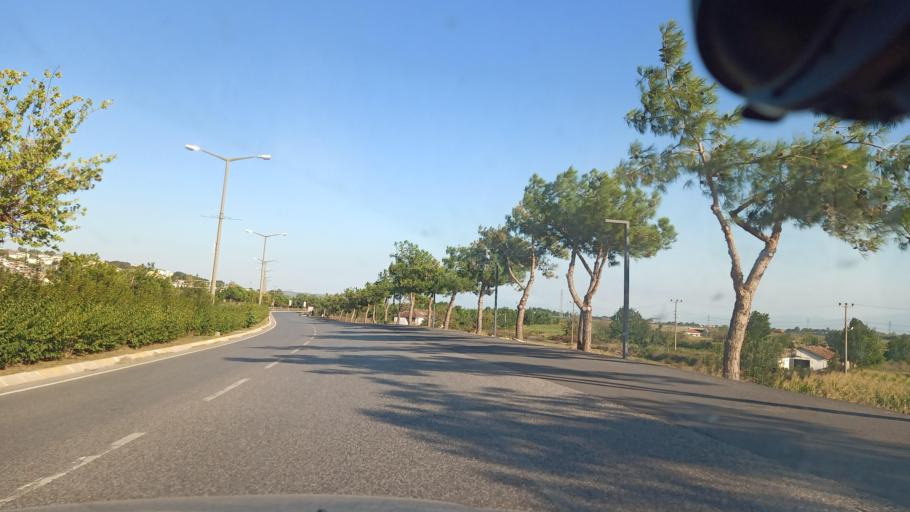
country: TR
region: Sakarya
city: Kazimpasa
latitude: 40.8496
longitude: 30.3191
